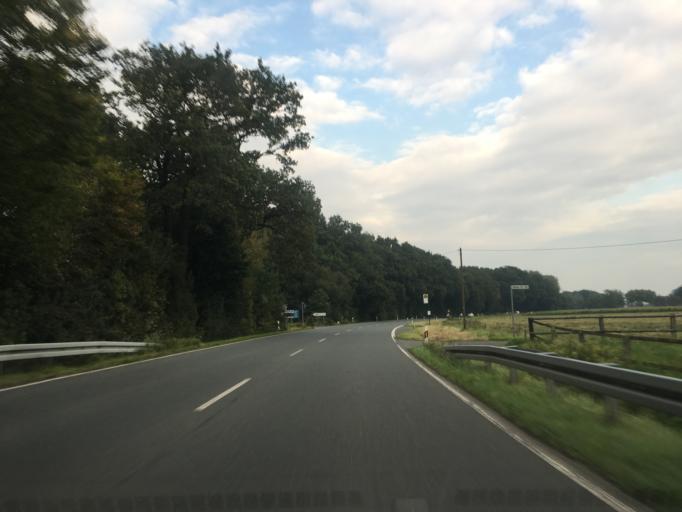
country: DE
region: North Rhine-Westphalia
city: Olfen
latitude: 51.7087
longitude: 7.4237
